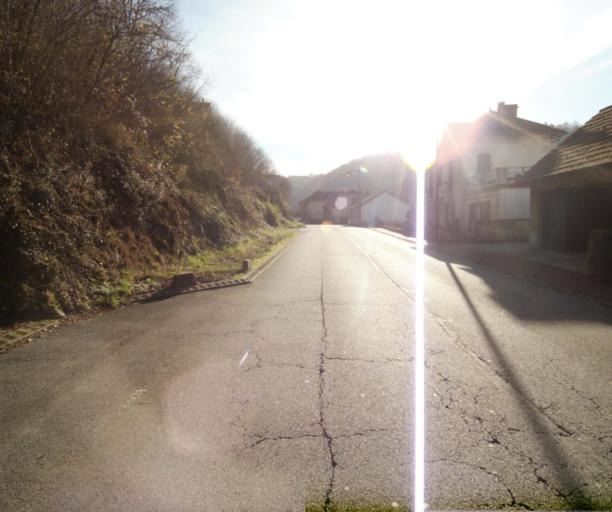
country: FR
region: Limousin
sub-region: Departement de la Correze
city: Laguenne
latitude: 45.2441
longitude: 1.7789
